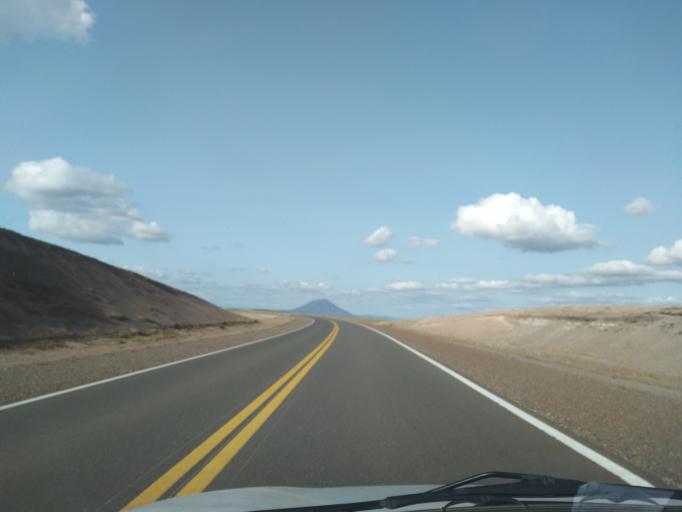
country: AR
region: Mendoza
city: Malargue
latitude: -34.8190
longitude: -69.2501
